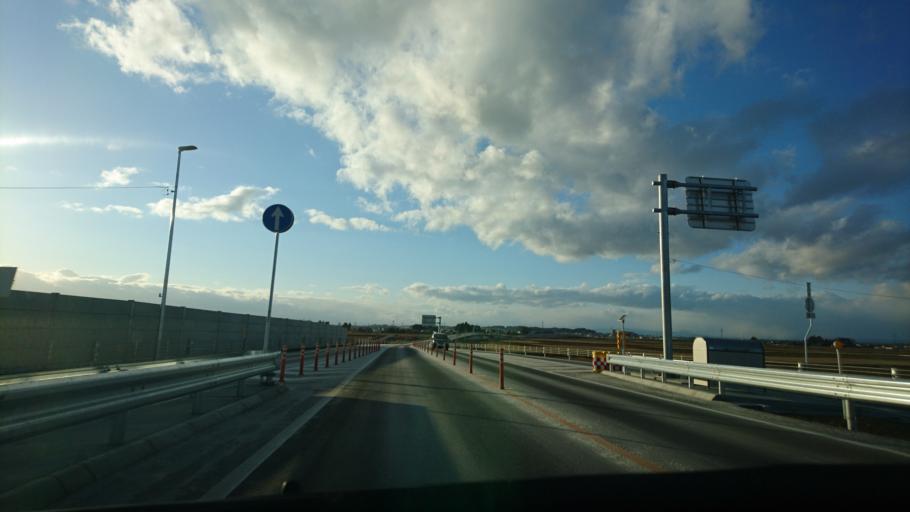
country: JP
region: Miyagi
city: Wakuya
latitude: 38.6863
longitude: 141.2315
